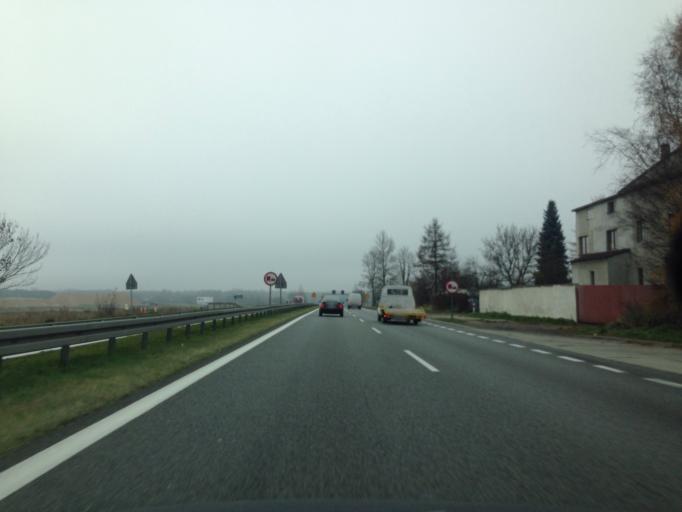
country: PL
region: Silesian Voivodeship
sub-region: Powiat bedzinski
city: Siewierz
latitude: 50.4991
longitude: 19.2018
